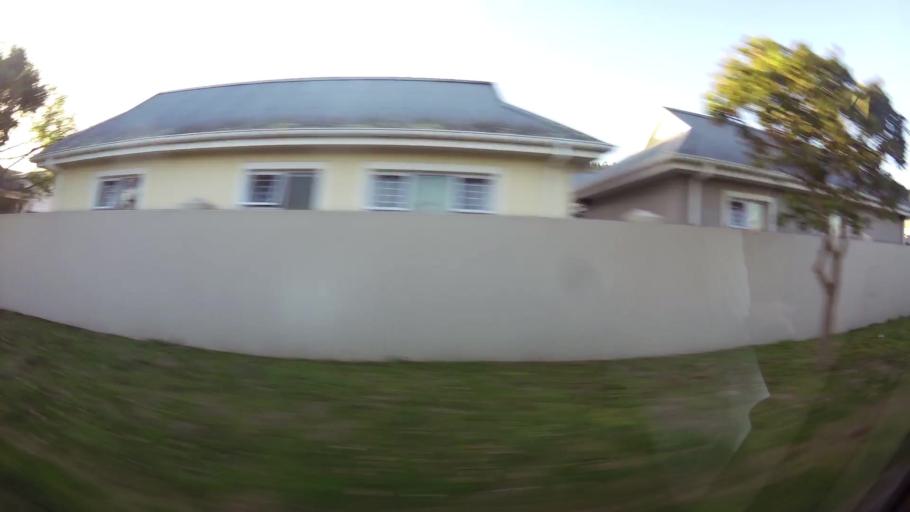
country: ZA
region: Western Cape
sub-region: Eden District Municipality
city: Knysna
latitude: -34.0126
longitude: 22.7927
